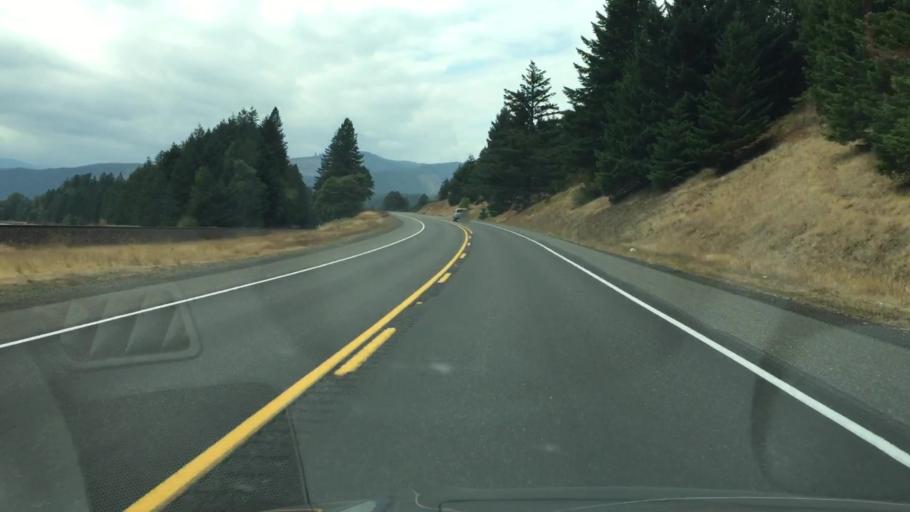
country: US
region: Washington
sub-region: Skamania County
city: Carson
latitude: 45.7073
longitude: -121.7655
